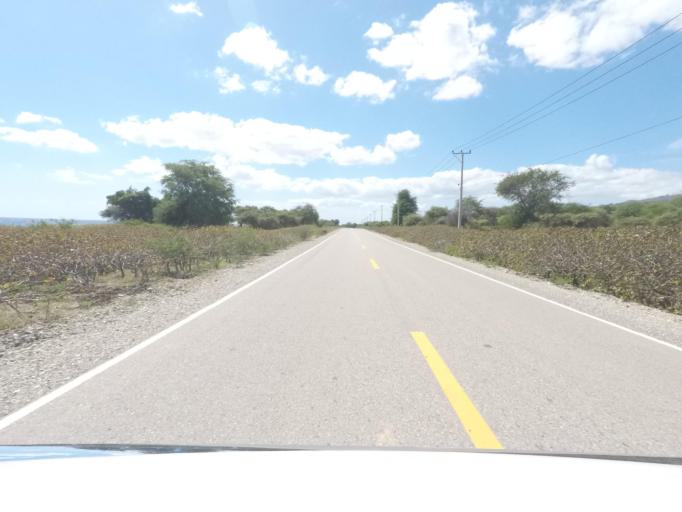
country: TL
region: Baucau
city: Baucau
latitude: -8.4578
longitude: 126.6163
